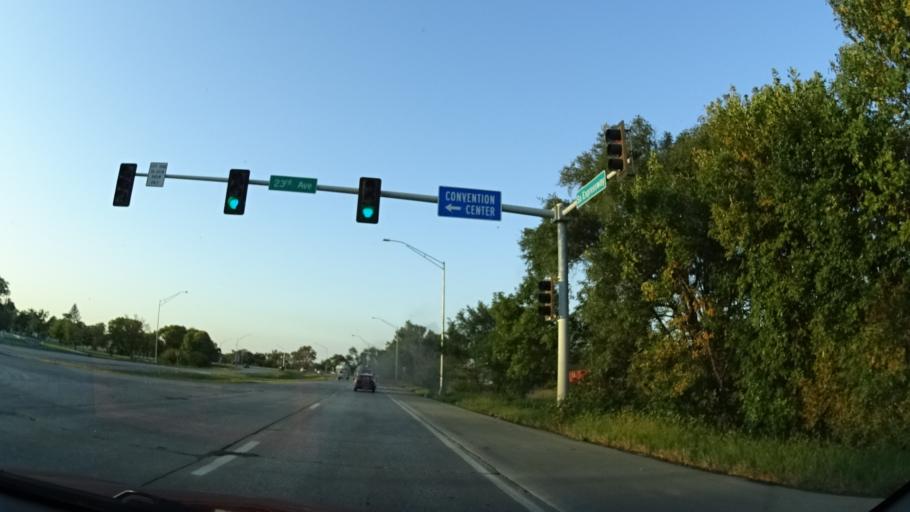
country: US
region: Iowa
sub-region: Pottawattamie County
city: Council Bluffs
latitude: 41.2391
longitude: -95.8512
